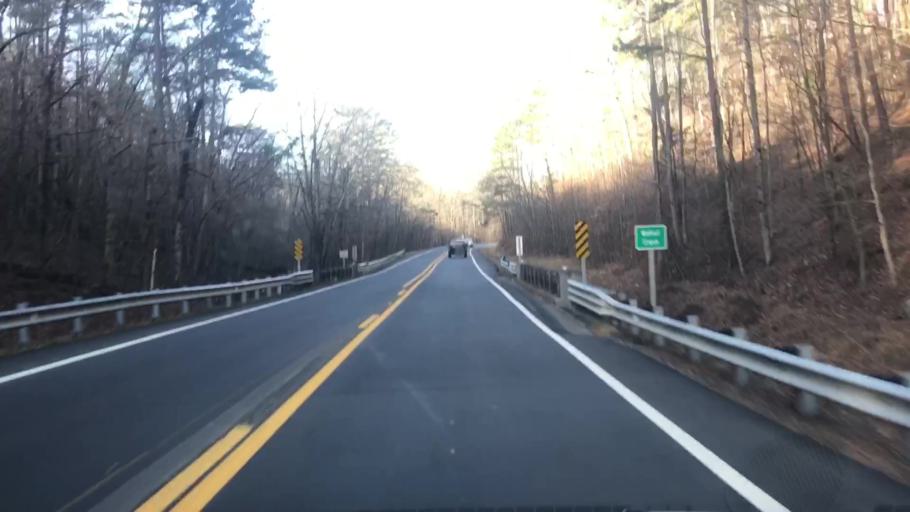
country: US
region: Arkansas
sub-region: Montgomery County
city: Mount Ida
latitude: 34.5236
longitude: -93.4083
